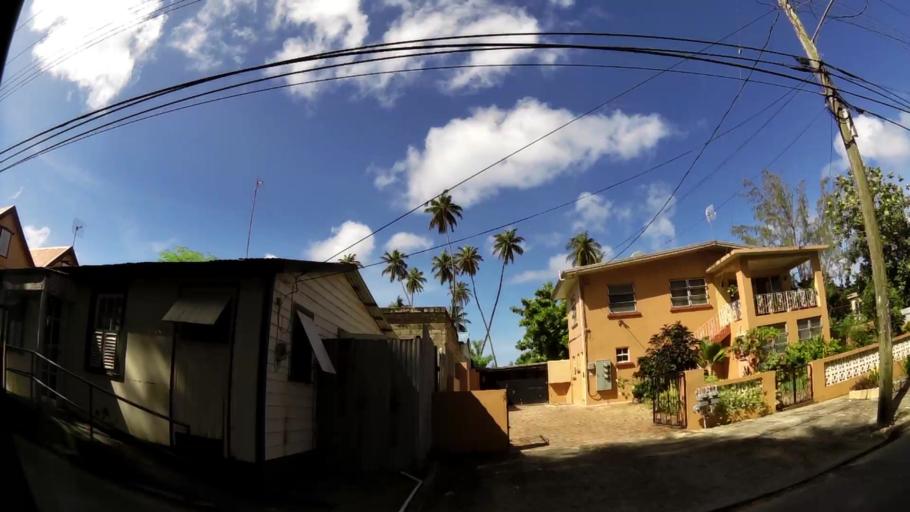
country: BB
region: Saint Peter
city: Speightstown
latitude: 13.2469
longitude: -59.6436
